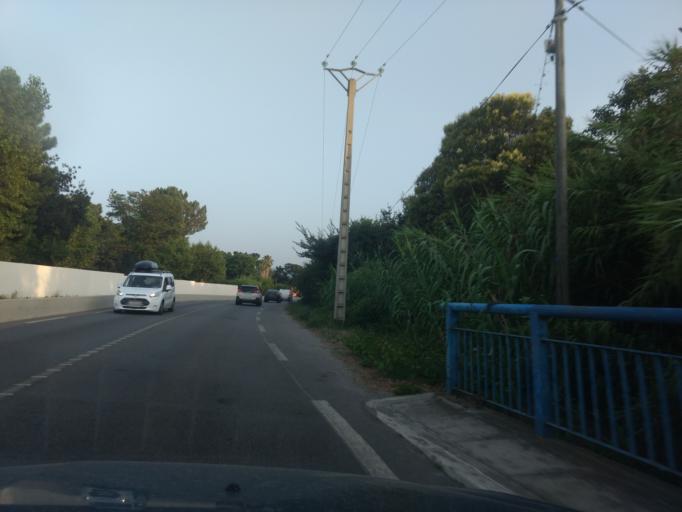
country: FR
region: Languedoc-Roussillon
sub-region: Departement des Pyrenees-Orientales
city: Argelers
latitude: 42.5823
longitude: 3.0324
